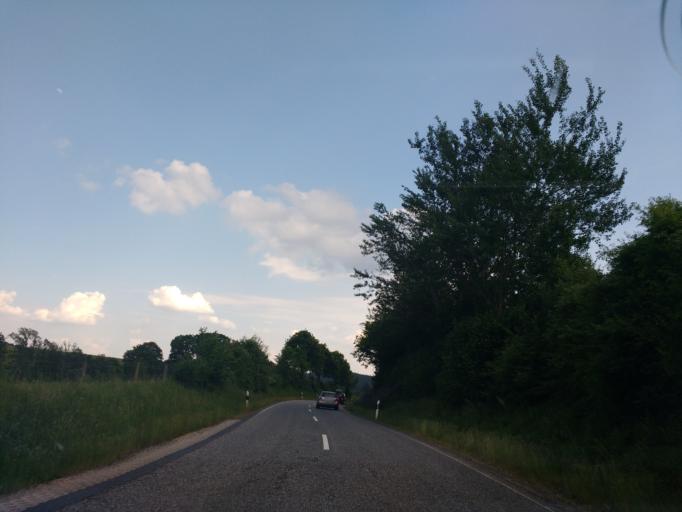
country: DE
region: Hesse
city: Rosenthal
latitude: 50.9290
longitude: 8.8407
